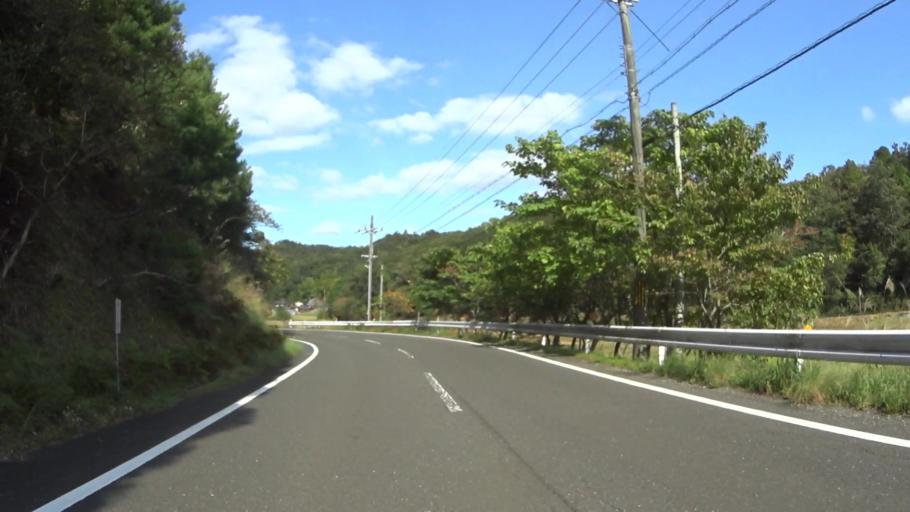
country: JP
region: Hyogo
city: Toyooka
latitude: 35.5582
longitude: 134.9797
